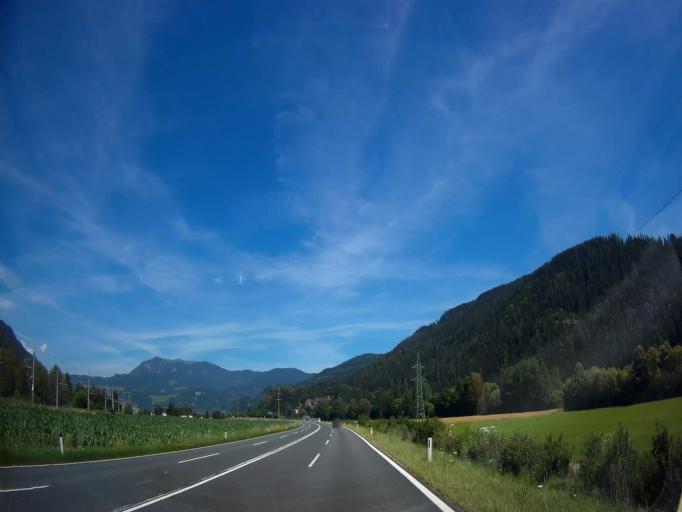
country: AT
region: Carinthia
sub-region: Politischer Bezirk Sankt Veit an der Glan
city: Friesach
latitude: 46.9445
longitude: 14.4232
